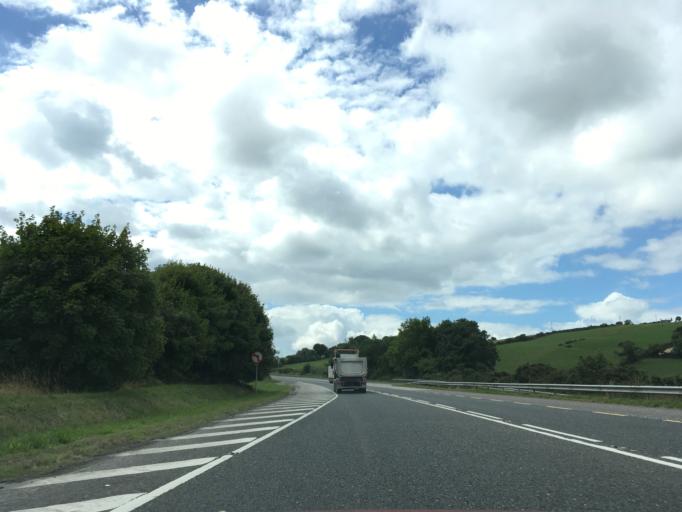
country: IE
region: Munster
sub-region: County Cork
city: Carrigaline
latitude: 51.8609
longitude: -8.4202
